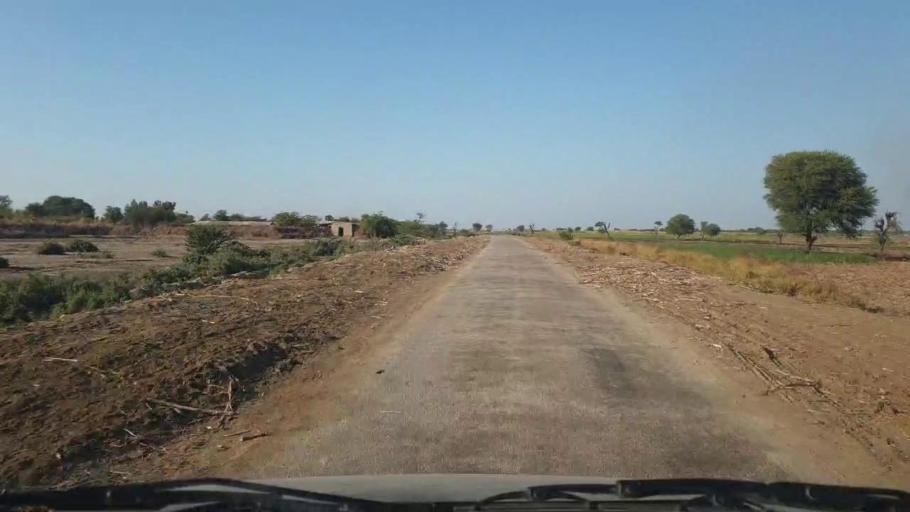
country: PK
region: Sindh
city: Samaro
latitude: 25.3455
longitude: 69.2994
